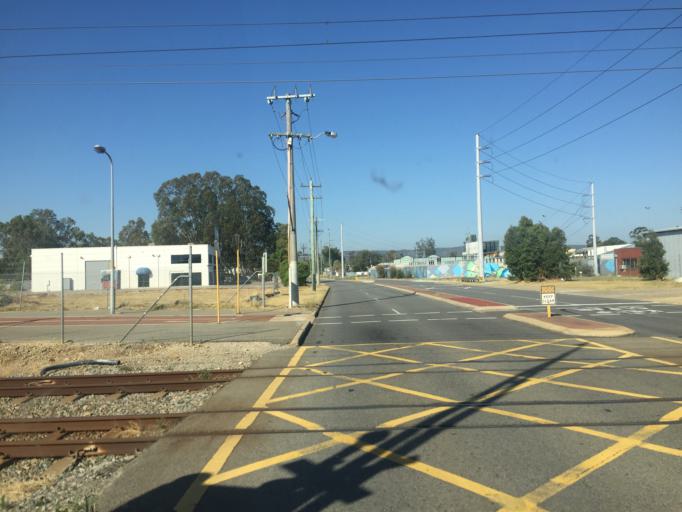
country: AU
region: Western Australia
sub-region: Gosnells
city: Maddington
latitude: -32.0454
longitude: 115.9768
